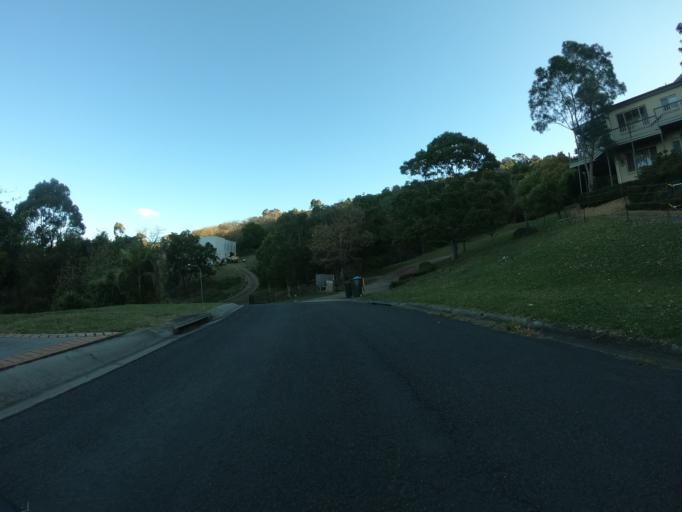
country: AU
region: New South Wales
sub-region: Wollongong
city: Mount Keira
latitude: -34.4224
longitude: 150.8445
